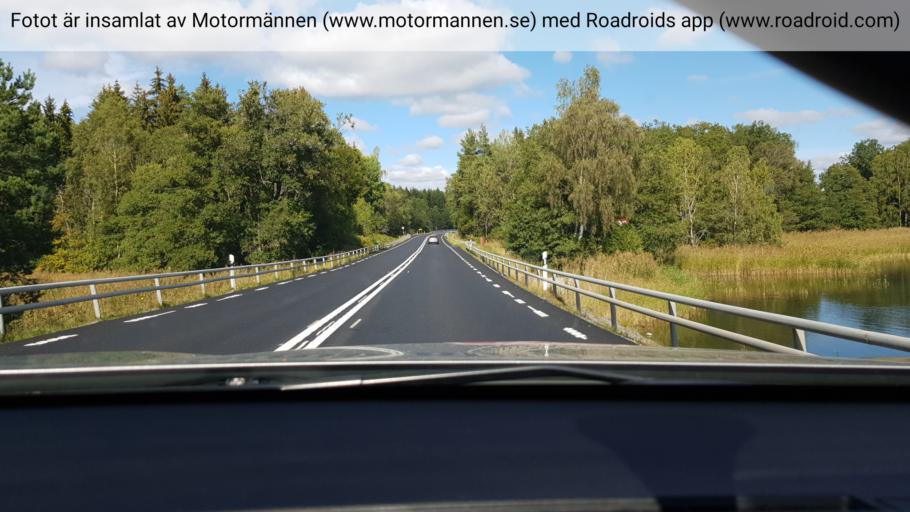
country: SE
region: Stockholm
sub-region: Lidingo
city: Brevik
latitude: 59.4317
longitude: 18.2198
